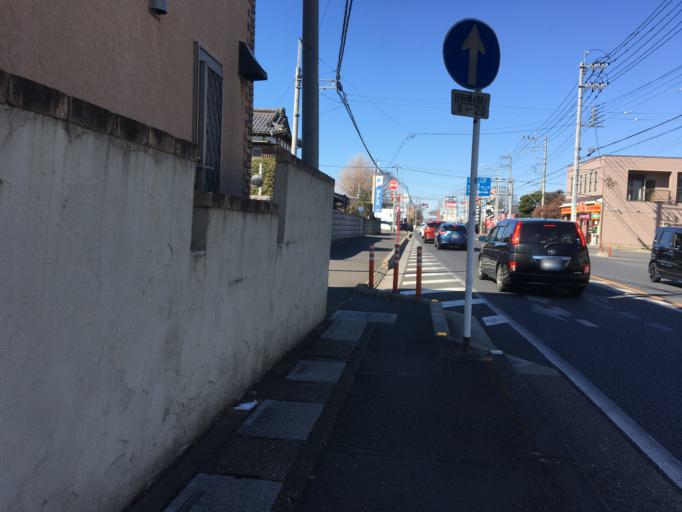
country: JP
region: Saitama
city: Oi
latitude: 35.8351
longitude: 139.5292
